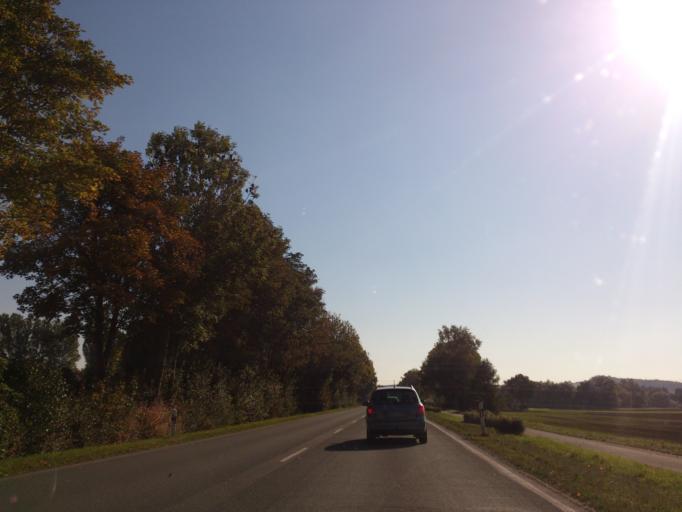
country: DE
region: North Rhine-Westphalia
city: Warburg
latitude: 51.5185
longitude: 9.0710
